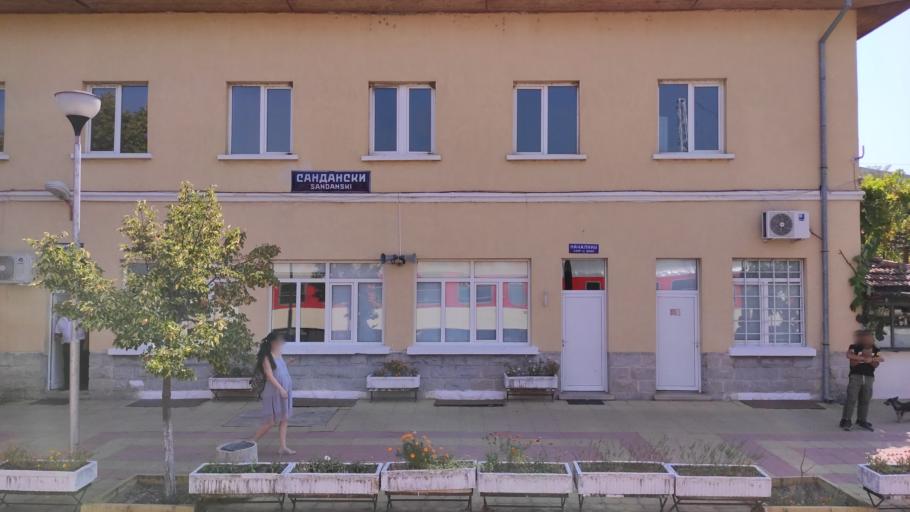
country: BG
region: Blagoevgrad
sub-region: Obshtina Sandanski
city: Sandanski
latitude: 41.5426
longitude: 23.2516
